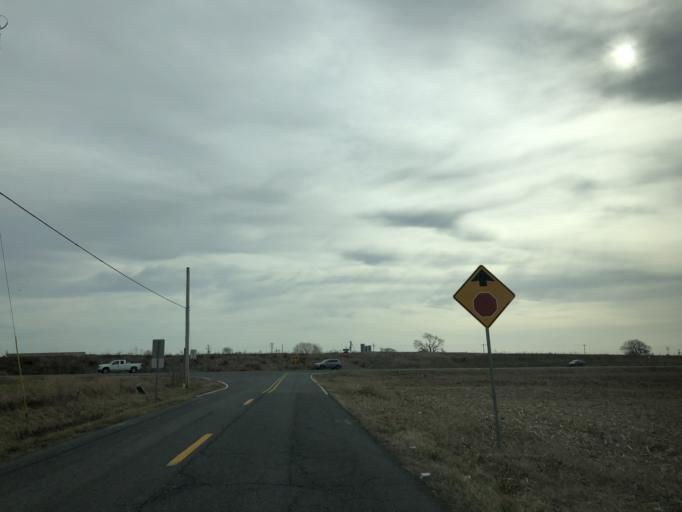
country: US
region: Delaware
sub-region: New Castle County
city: Middletown
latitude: 39.4367
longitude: -75.7604
